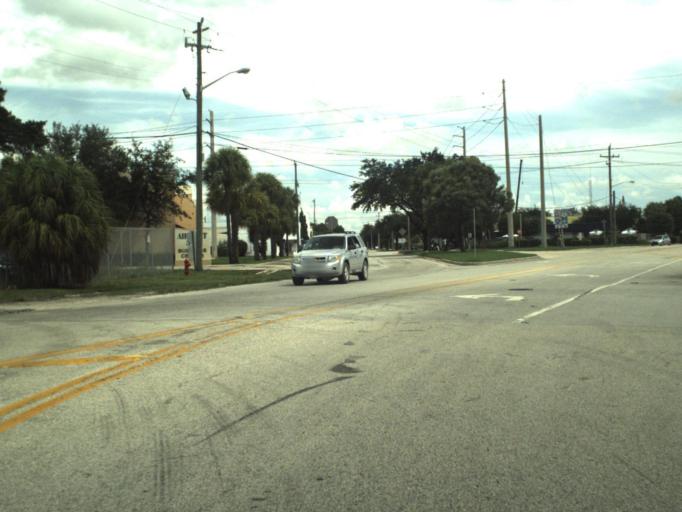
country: US
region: Florida
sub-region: Broward County
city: Dania Beach
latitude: 26.0822
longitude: -80.1383
